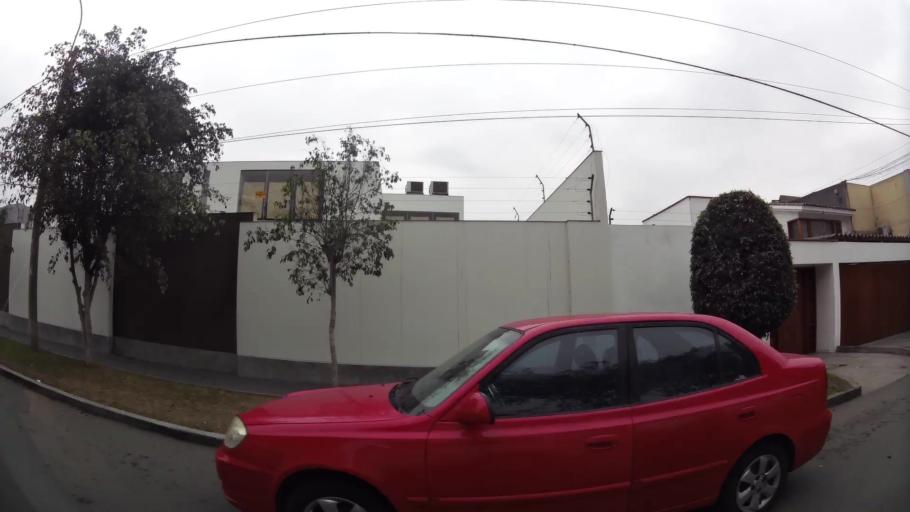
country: PE
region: Lima
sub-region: Lima
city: La Molina
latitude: -12.0856
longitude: -76.9241
